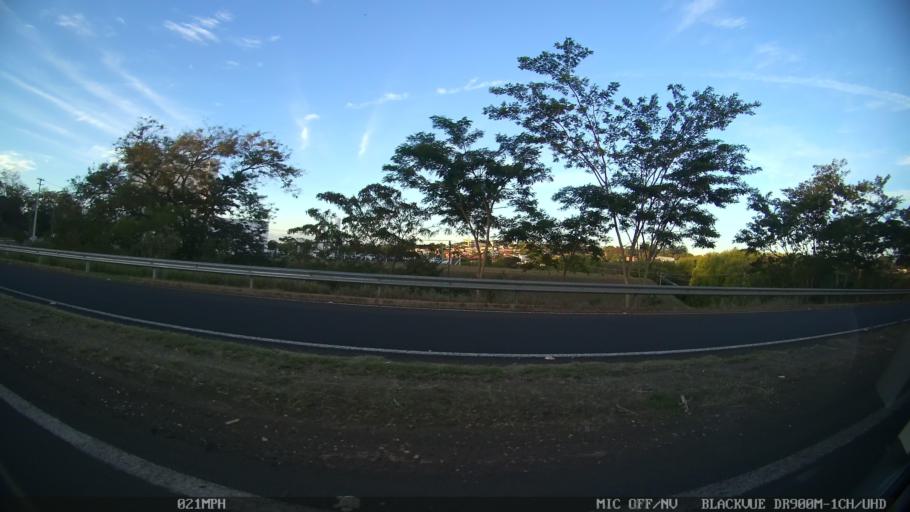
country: BR
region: Sao Paulo
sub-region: Catanduva
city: Catanduva
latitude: -21.1595
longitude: -48.9852
